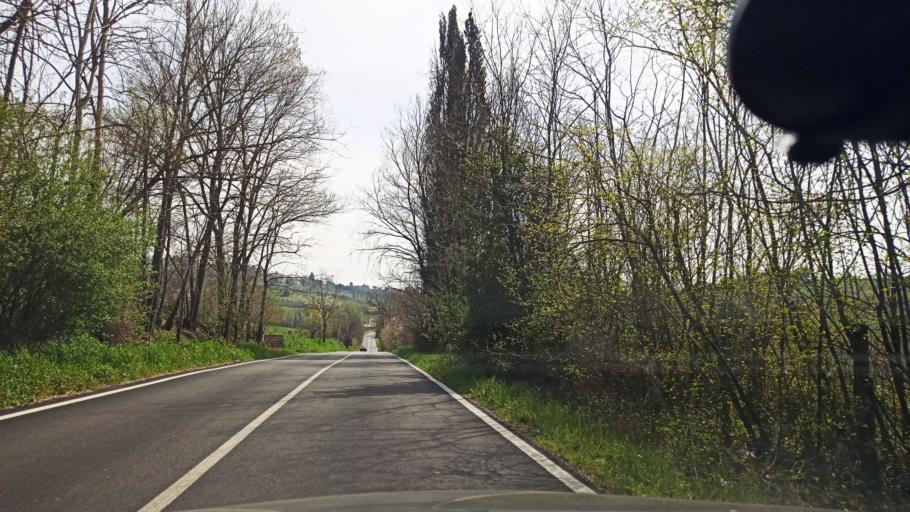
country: IT
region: Latium
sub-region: Provincia di Rieti
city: Cantalupo in Sabina
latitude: 42.3230
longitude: 12.6428
